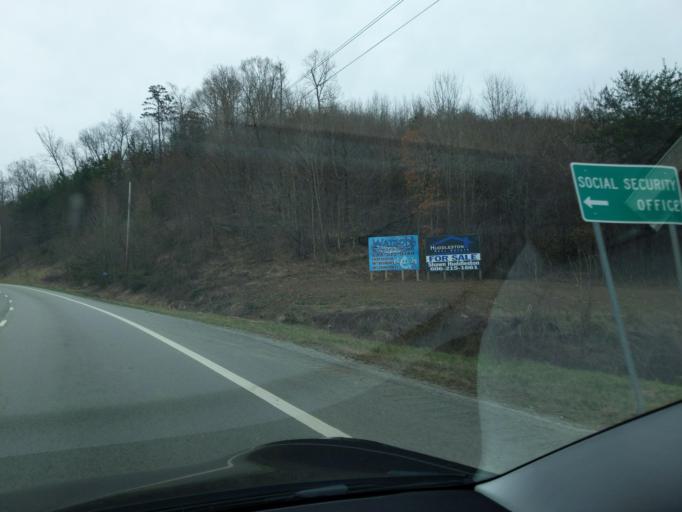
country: US
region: Kentucky
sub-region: Whitley County
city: Corbin
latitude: 36.9191
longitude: -84.1139
